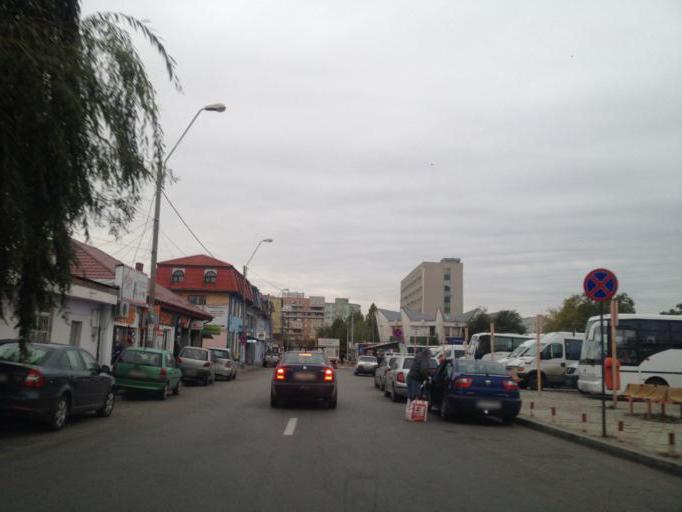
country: RO
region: Dolj
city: Craiova
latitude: 44.3273
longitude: 23.8188
